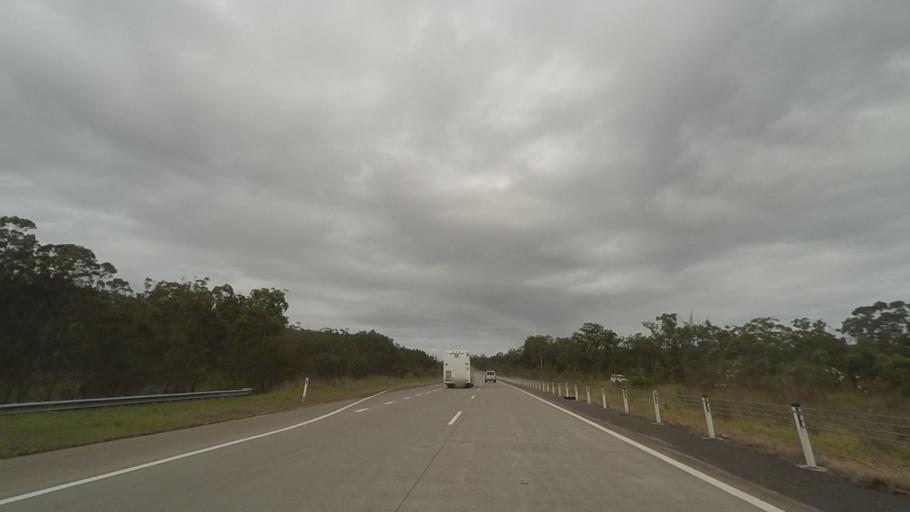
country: AU
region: New South Wales
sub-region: Port Stephens Shire
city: Port Stephens
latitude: -32.6224
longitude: 152.0643
